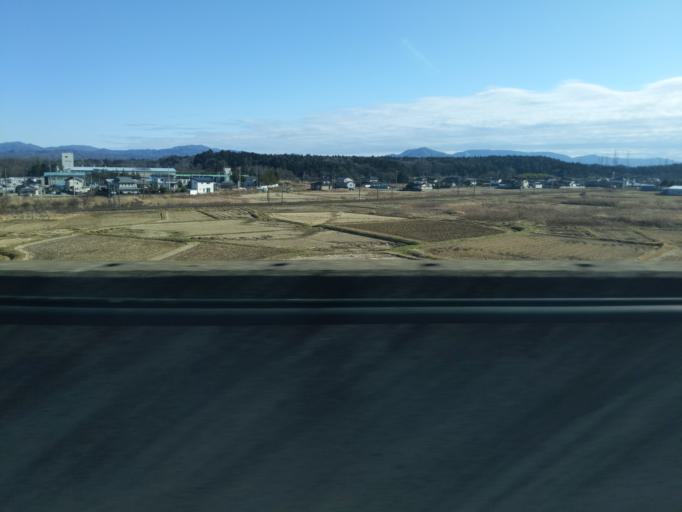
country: JP
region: Fukushima
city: Koriyama
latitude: 37.3429
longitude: 140.3682
